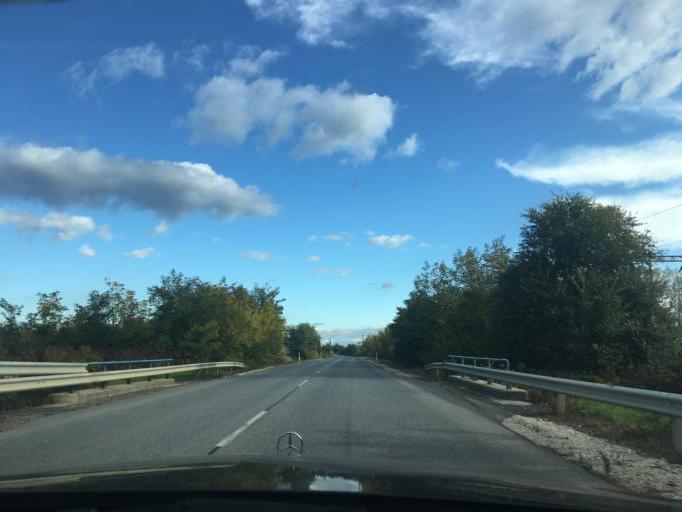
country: HU
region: Borsod-Abauj-Zemplen
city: Encs
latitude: 48.4012
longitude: 21.1675
